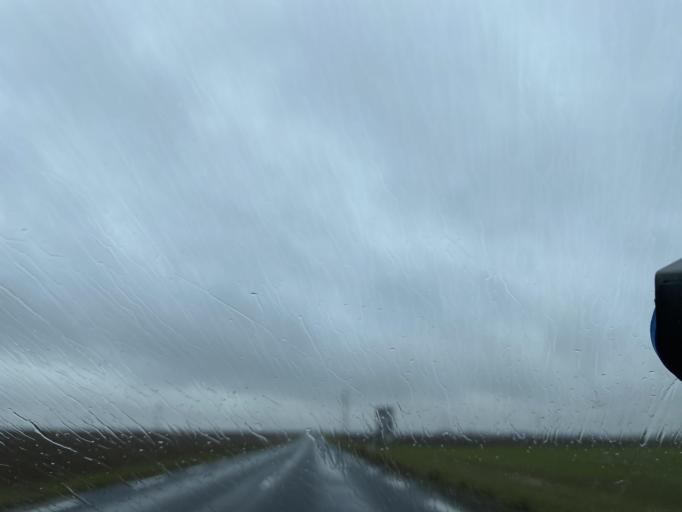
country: FR
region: Centre
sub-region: Departement d'Eure-et-Loir
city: Janville
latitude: 48.1992
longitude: 1.8262
